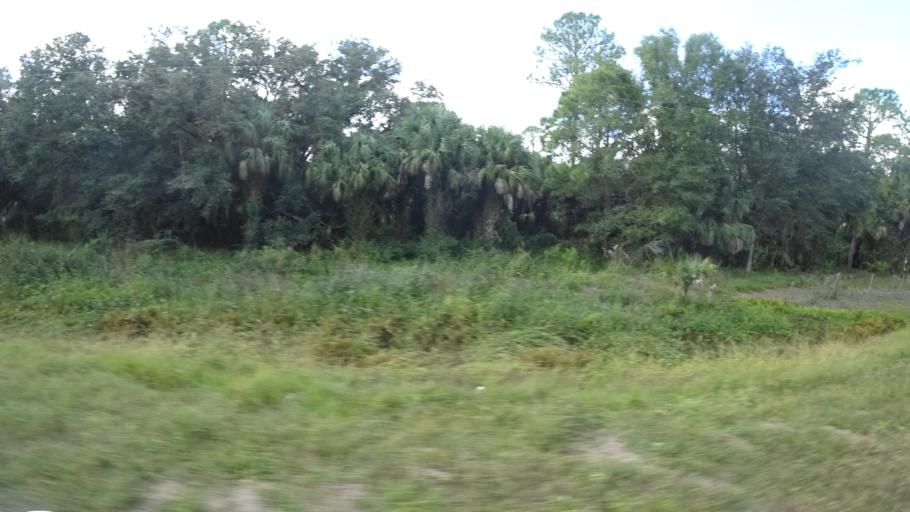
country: US
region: Florida
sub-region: Sarasota County
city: North Port
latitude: 27.2195
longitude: -82.1221
